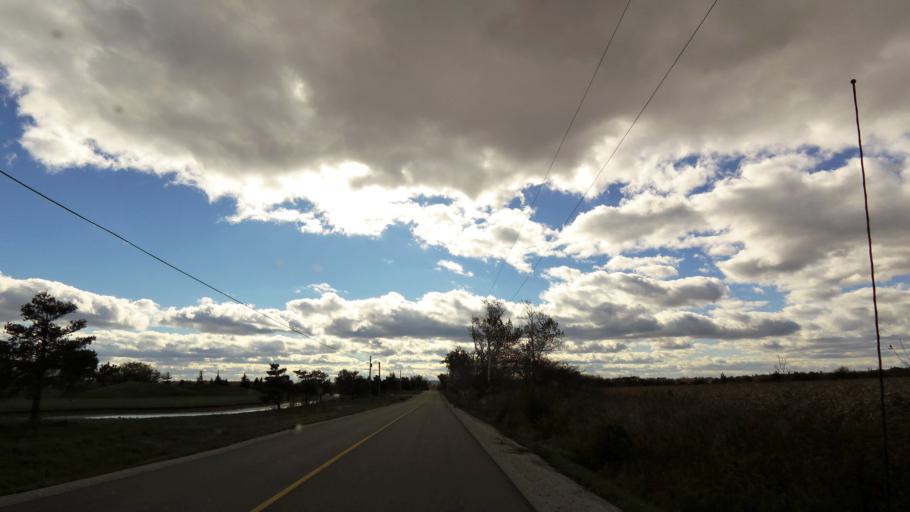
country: CA
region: Ontario
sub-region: Halton
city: Milton
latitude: 43.4850
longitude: -79.7882
